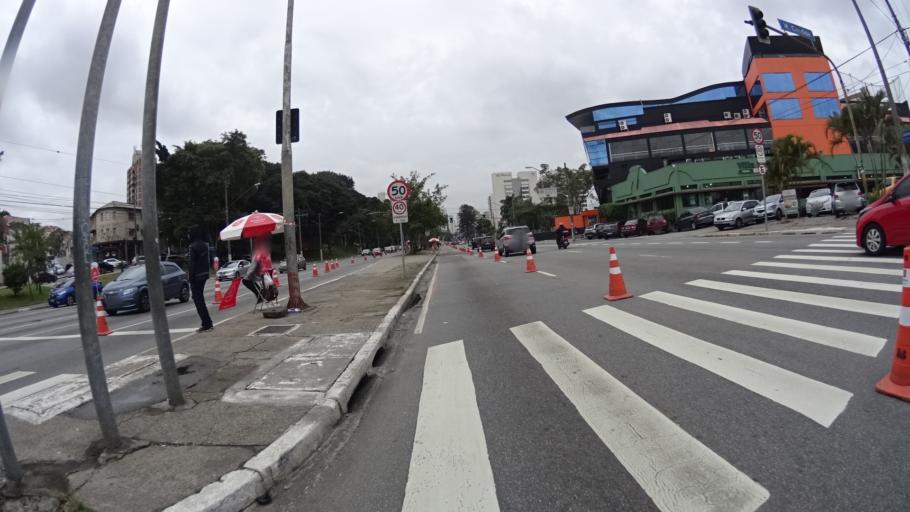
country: BR
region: Sao Paulo
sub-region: Sao Paulo
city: Sao Paulo
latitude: -23.5007
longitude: -46.6148
